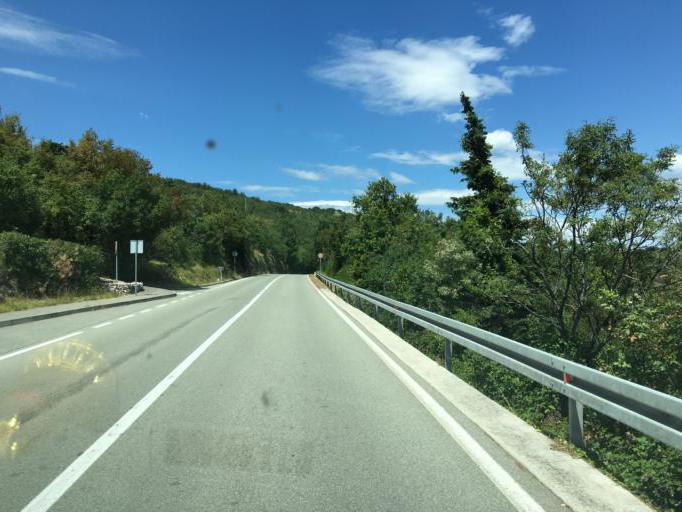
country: HR
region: Istarska
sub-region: Grad Labin
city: Rabac
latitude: 45.1643
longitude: 14.2233
